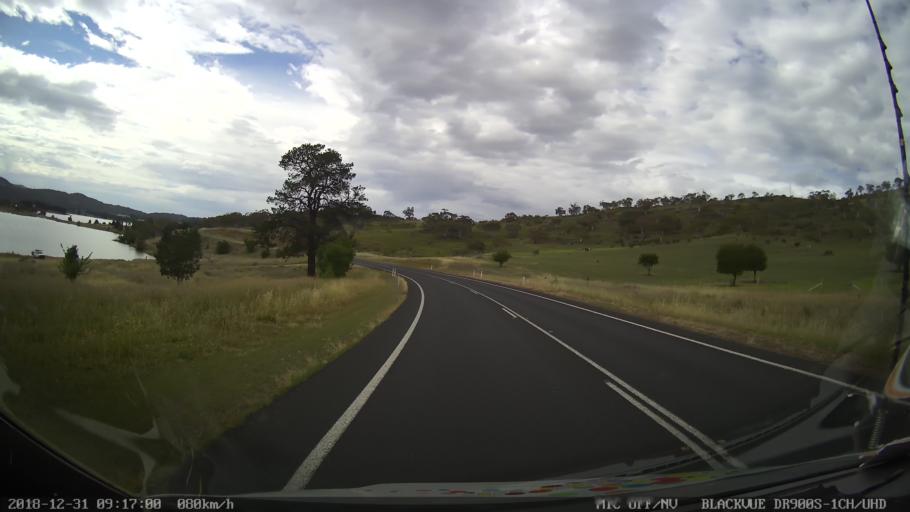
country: AU
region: New South Wales
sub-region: Snowy River
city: Jindabyne
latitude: -36.4026
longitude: 148.5971
